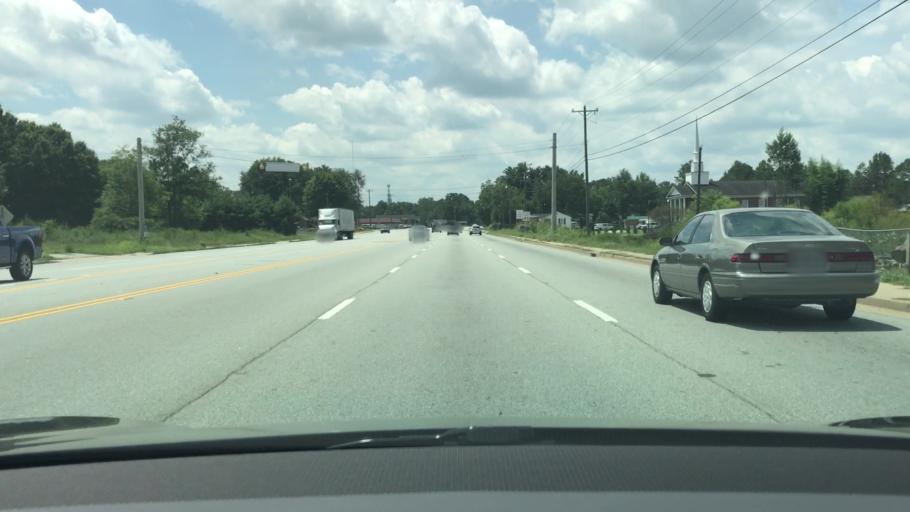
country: US
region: South Carolina
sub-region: Greenville County
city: Berea
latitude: 34.9028
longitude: -82.4624
